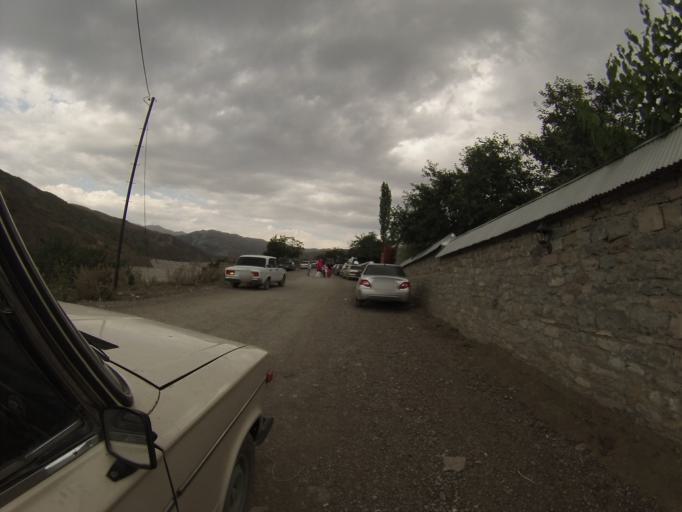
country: AZ
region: Ismayilli
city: Basqal
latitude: 40.8456
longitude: 48.3803
